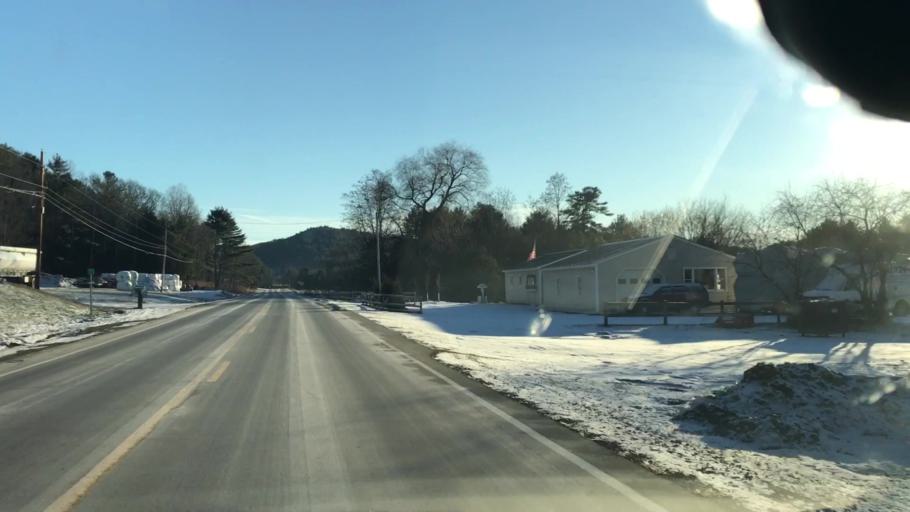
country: US
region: New Hampshire
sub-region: Grafton County
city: Lyme Town Offices
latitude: 43.8555
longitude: -72.1556
